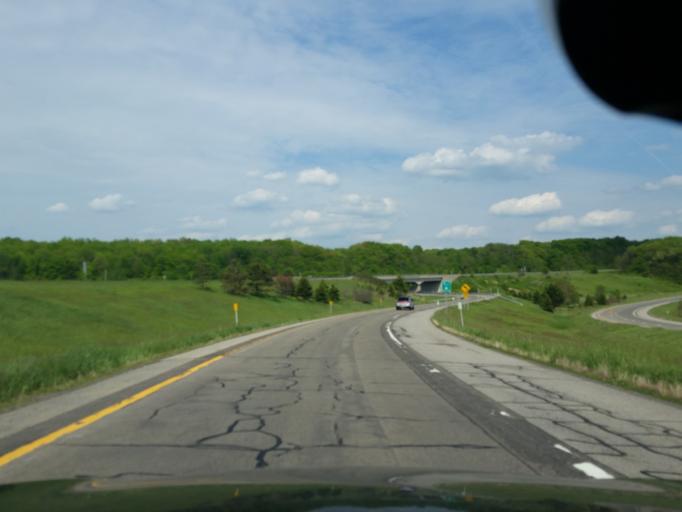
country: US
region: New York
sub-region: Chautauqua County
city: Lakewood
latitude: 42.1533
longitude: -79.3777
